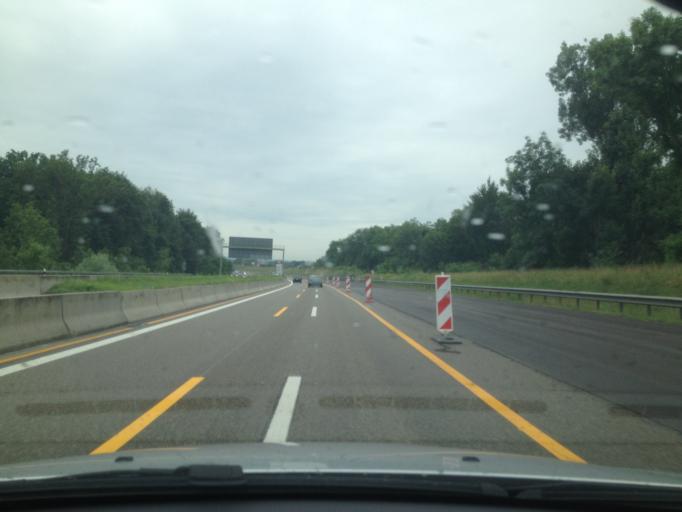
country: DE
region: Bavaria
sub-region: Swabia
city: Leipheim
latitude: 48.4498
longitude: 10.2037
